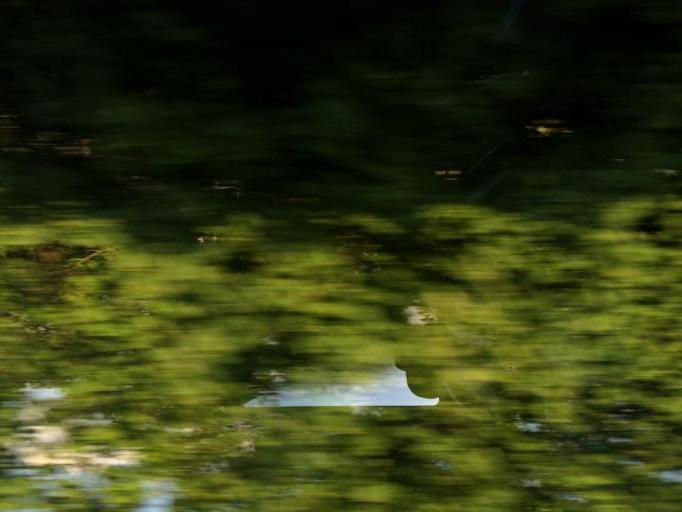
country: DE
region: North Rhine-Westphalia
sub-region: Regierungsbezirk Dusseldorf
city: Hochfeld
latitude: 51.3863
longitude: 6.7755
